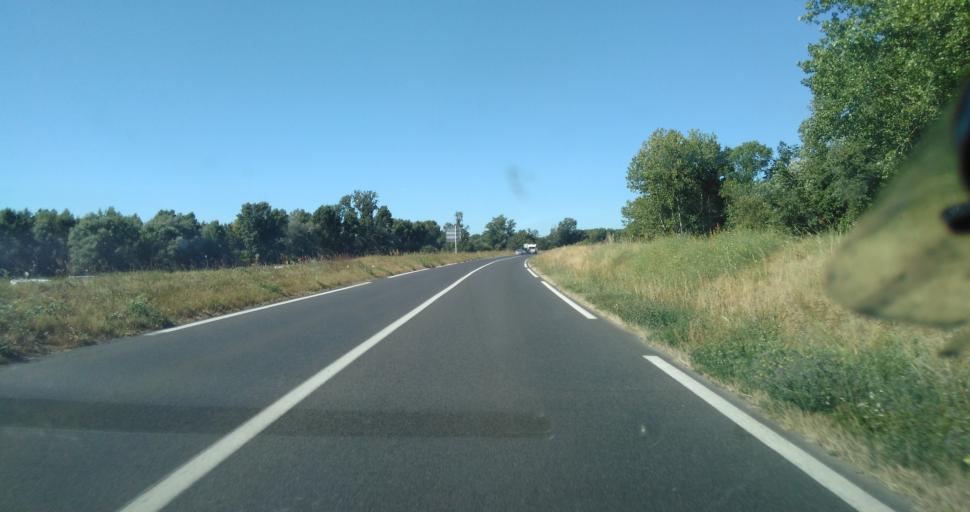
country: FR
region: Centre
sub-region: Departement d'Indre-et-Loire
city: Poce-sur-Cisse
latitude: 47.4289
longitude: 1.0032
